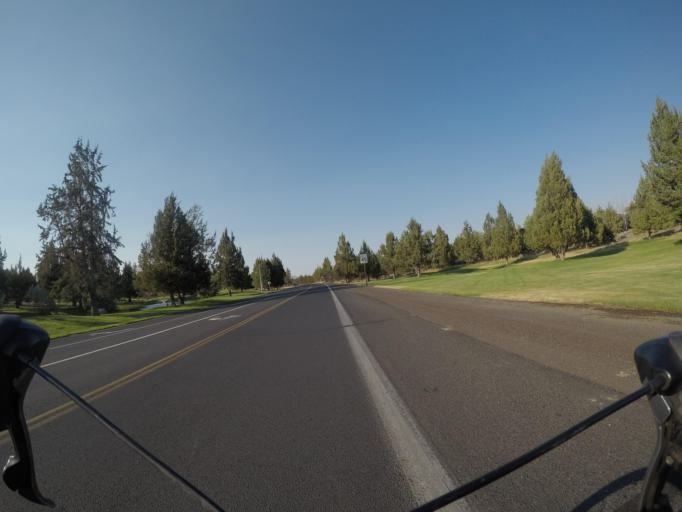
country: US
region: Oregon
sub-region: Deschutes County
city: Redmond
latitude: 44.2620
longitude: -121.2648
